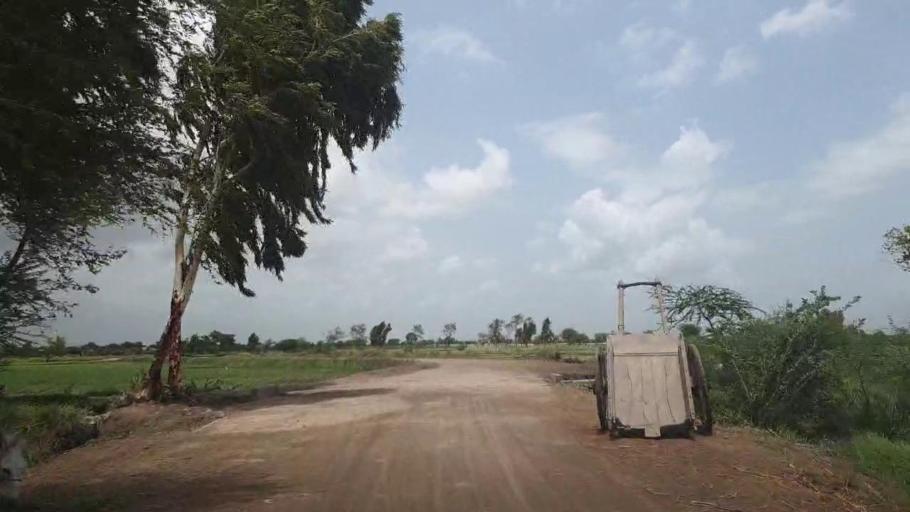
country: PK
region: Sindh
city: Badin
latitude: 24.6656
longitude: 68.9061
